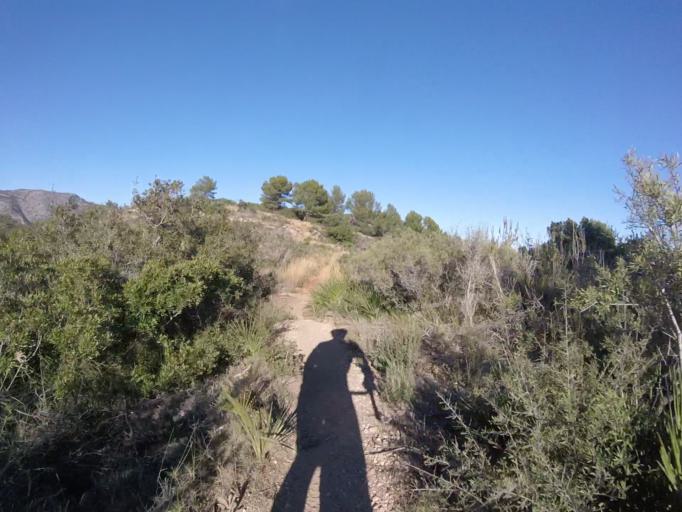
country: ES
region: Valencia
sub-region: Provincia de Castello
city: Orpesa/Oropesa del Mar
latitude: 40.1136
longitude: 0.1167
